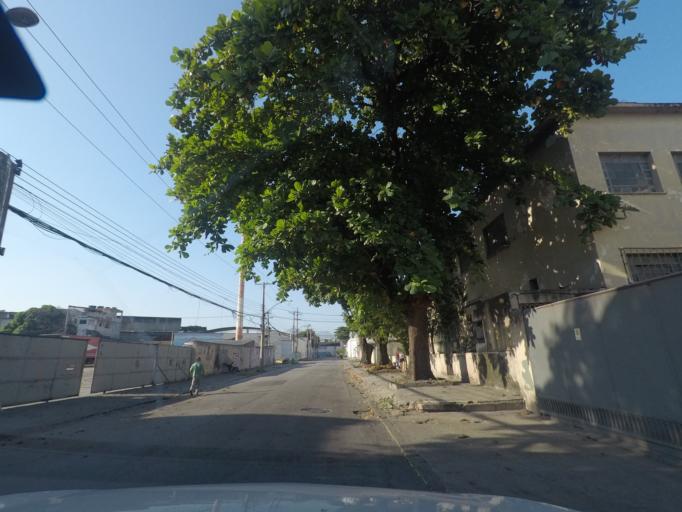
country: BR
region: Rio de Janeiro
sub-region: Rio De Janeiro
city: Rio de Janeiro
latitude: -22.8442
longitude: -43.2566
